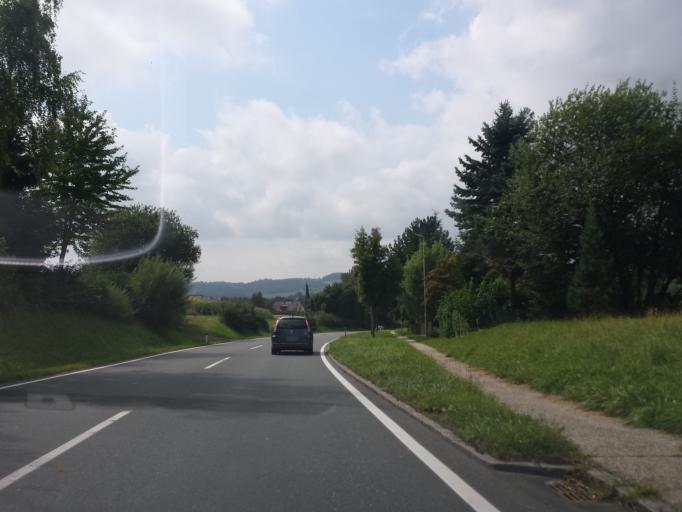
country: AT
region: Styria
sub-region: Politischer Bezirk Deutschlandsberg
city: Stainz
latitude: 46.9024
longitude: 15.2728
